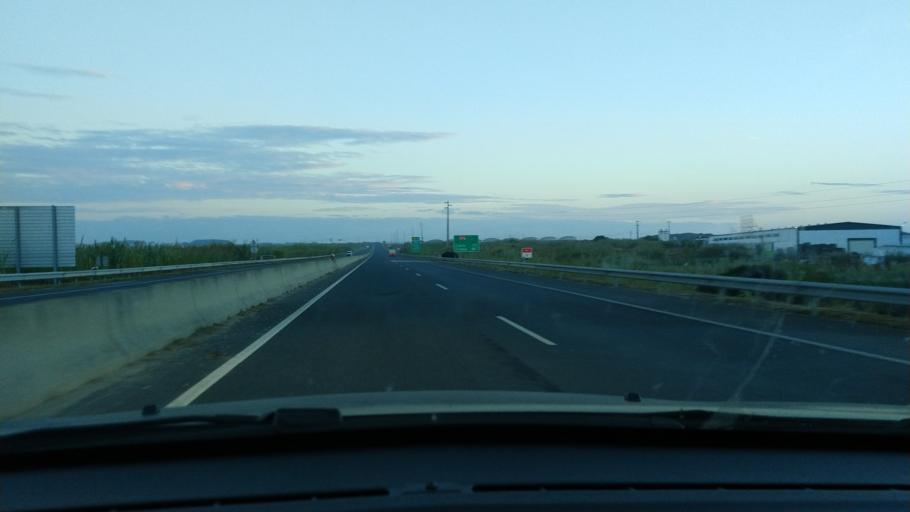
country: PT
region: Leiria
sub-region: Peniche
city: Atouguia da Baleia
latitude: 39.3438
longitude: -9.3402
